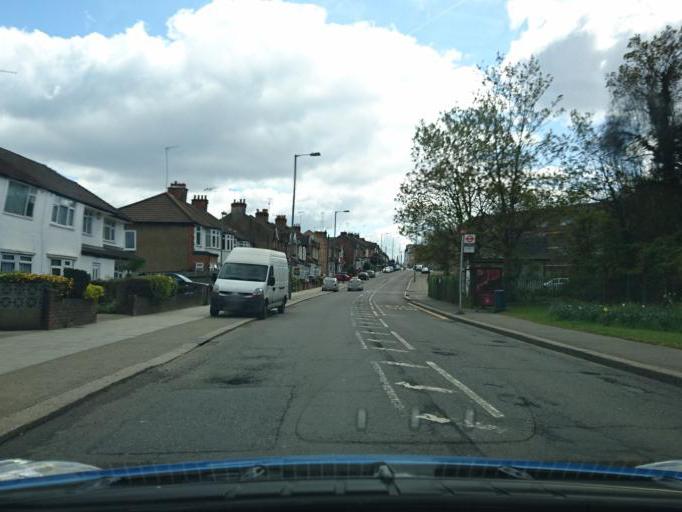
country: GB
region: England
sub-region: Greater London
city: Wood Green
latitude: 51.6193
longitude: -0.1456
